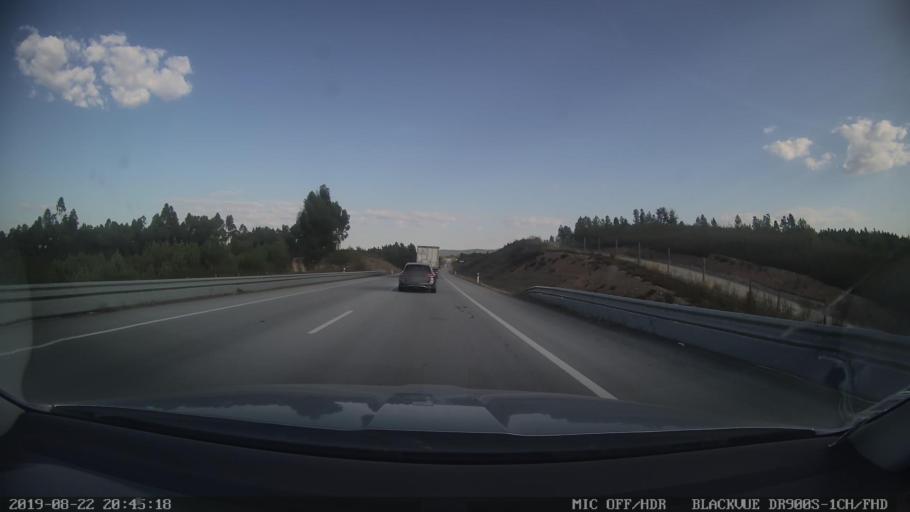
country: PT
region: Castelo Branco
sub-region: Proenca-A-Nova
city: Proenca-a-Nova
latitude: 39.7154
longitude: -7.8648
